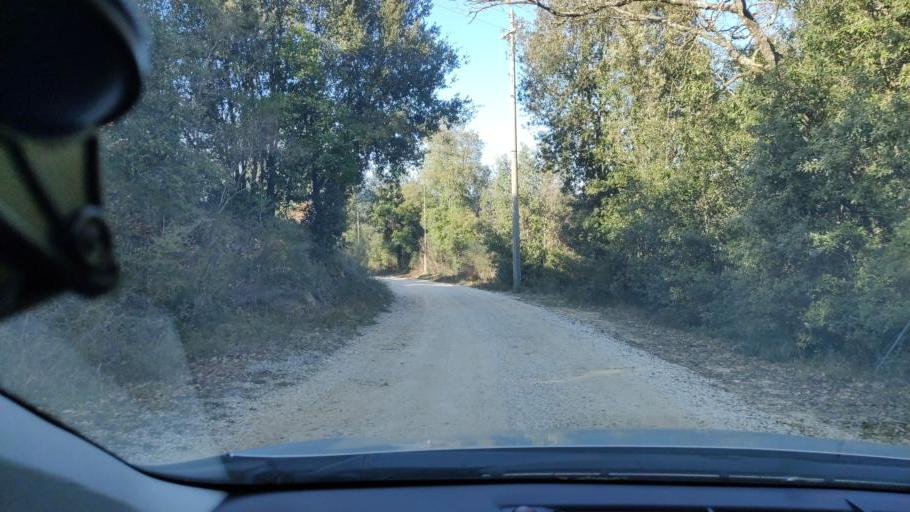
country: IT
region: Umbria
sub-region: Provincia di Terni
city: Amelia
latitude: 42.5625
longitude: 12.4414
